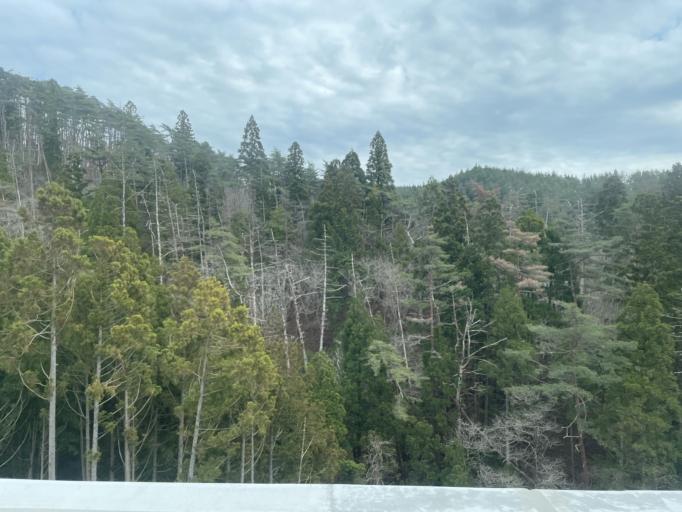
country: JP
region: Iwate
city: Ofunato
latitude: 38.9203
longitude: 141.5941
